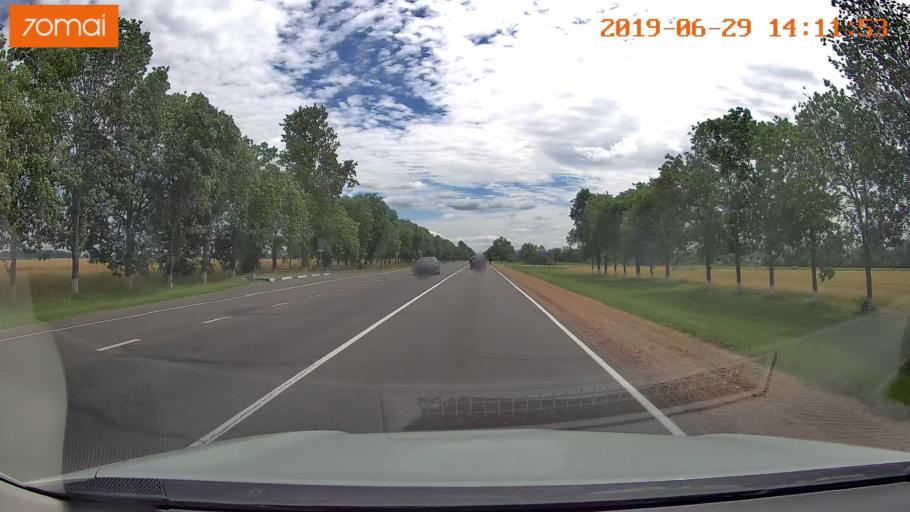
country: BY
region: Minsk
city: Salihorsk
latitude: 52.8154
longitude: 27.5050
